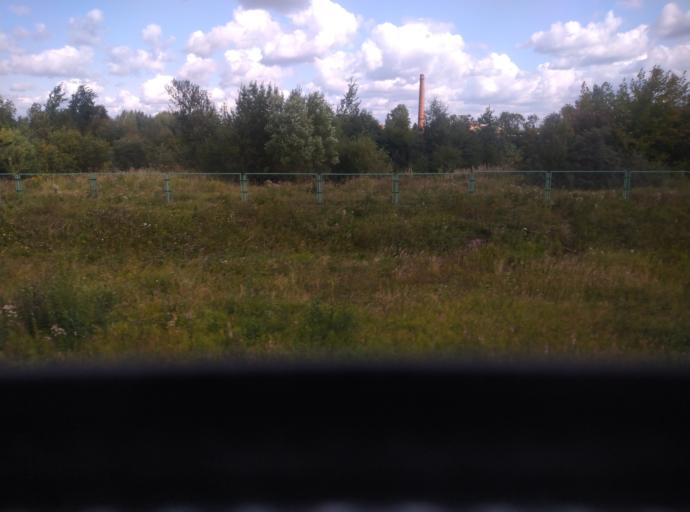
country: RU
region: St.-Petersburg
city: Kolpino
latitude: 59.7585
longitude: 30.5942
